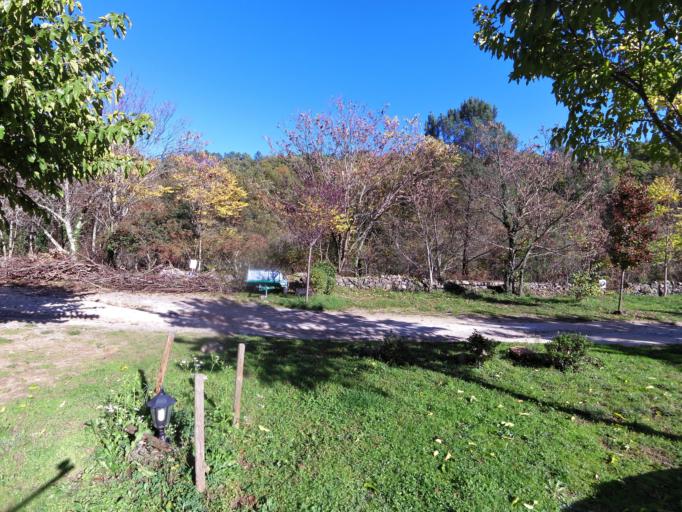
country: FR
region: Rhone-Alpes
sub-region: Departement de l'Ardeche
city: Largentiere
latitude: 44.5329
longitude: 4.2884
